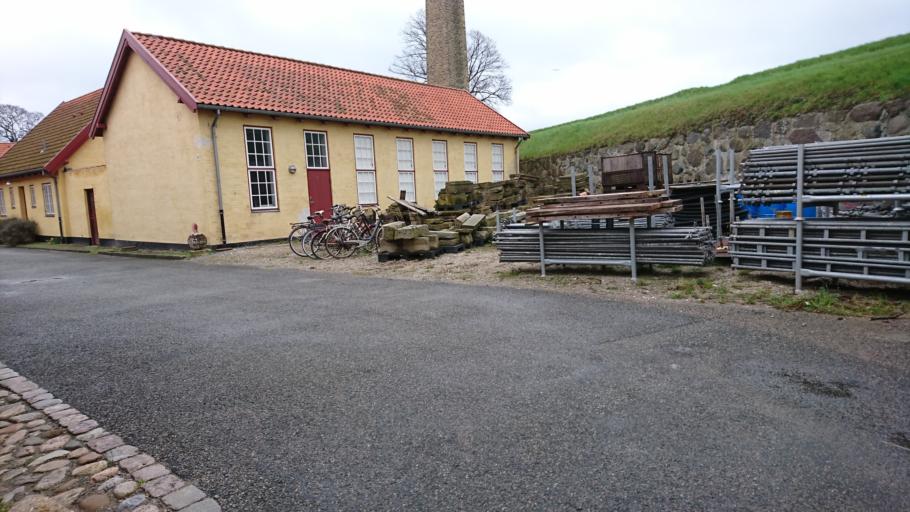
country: DK
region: Capital Region
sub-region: Helsingor Kommune
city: Helsingor
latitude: 56.0380
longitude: 12.6202
